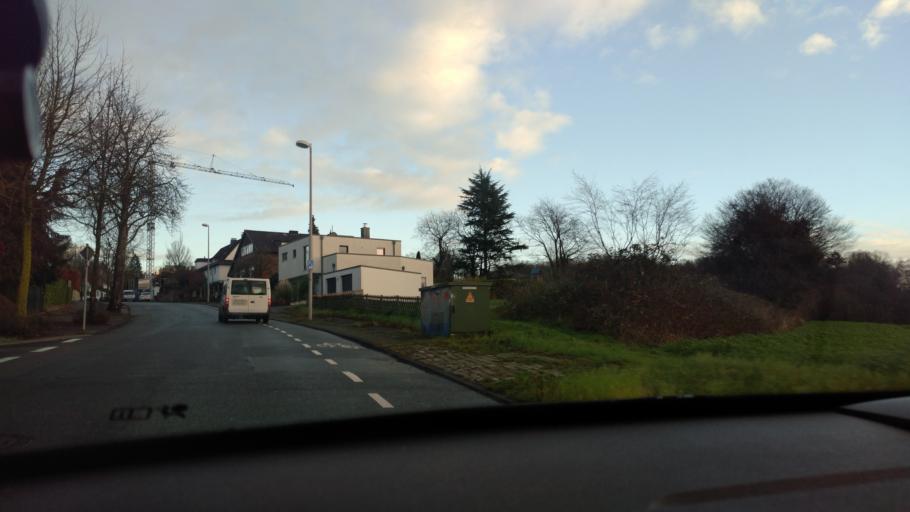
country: DE
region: North Rhine-Westphalia
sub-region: Regierungsbezirk Dusseldorf
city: Muelheim (Ruhr)
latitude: 51.4055
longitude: 6.9029
